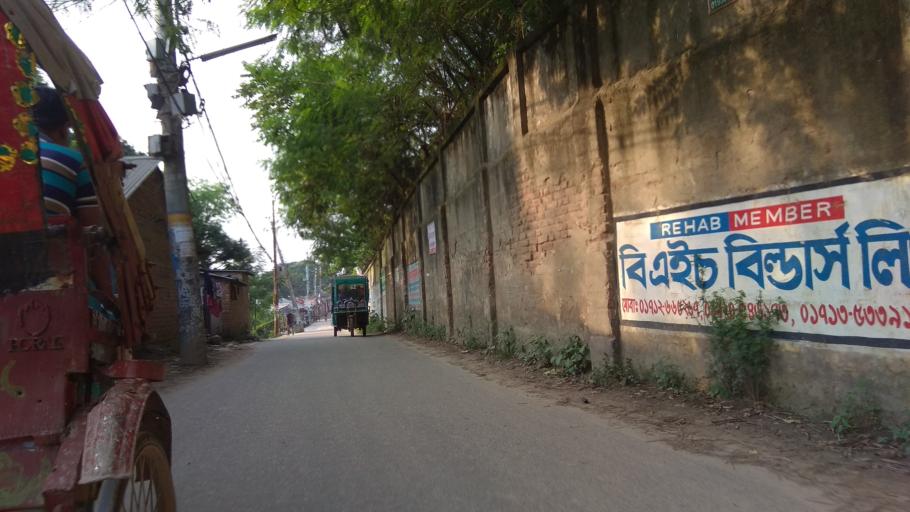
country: BD
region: Dhaka
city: Tungi
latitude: 23.8405
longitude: 90.3876
